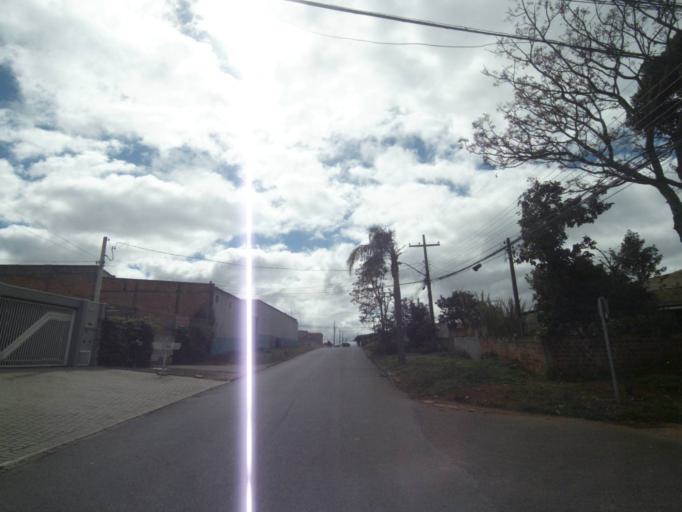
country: BR
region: Parana
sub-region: Sao Jose Dos Pinhais
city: Sao Jose dos Pinhais
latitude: -25.5356
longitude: -49.2897
